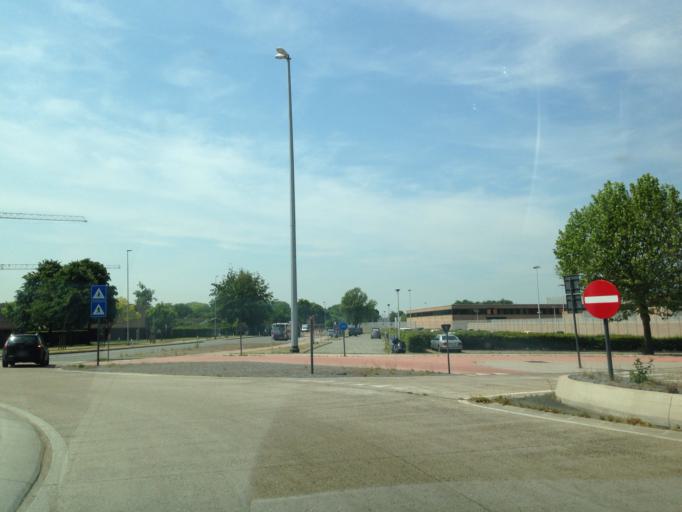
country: BE
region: Flanders
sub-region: Provincie West-Vlaanderen
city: Brugge
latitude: 51.2062
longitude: 3.1925
